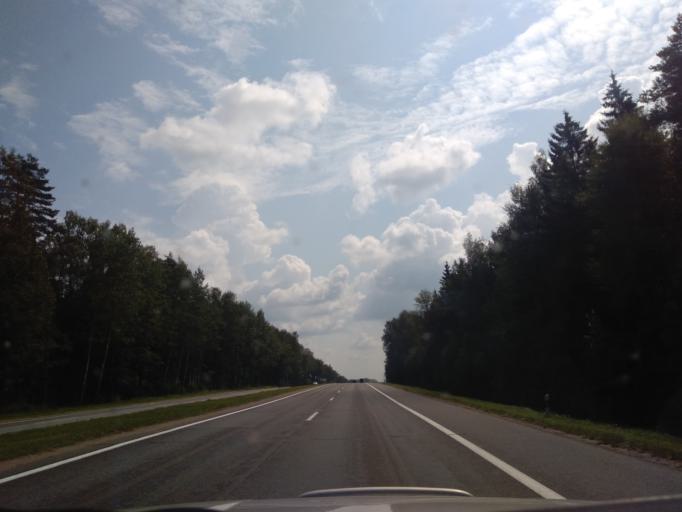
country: BY
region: Minsk
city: Rakaw
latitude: 54.0170
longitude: 26.8982
